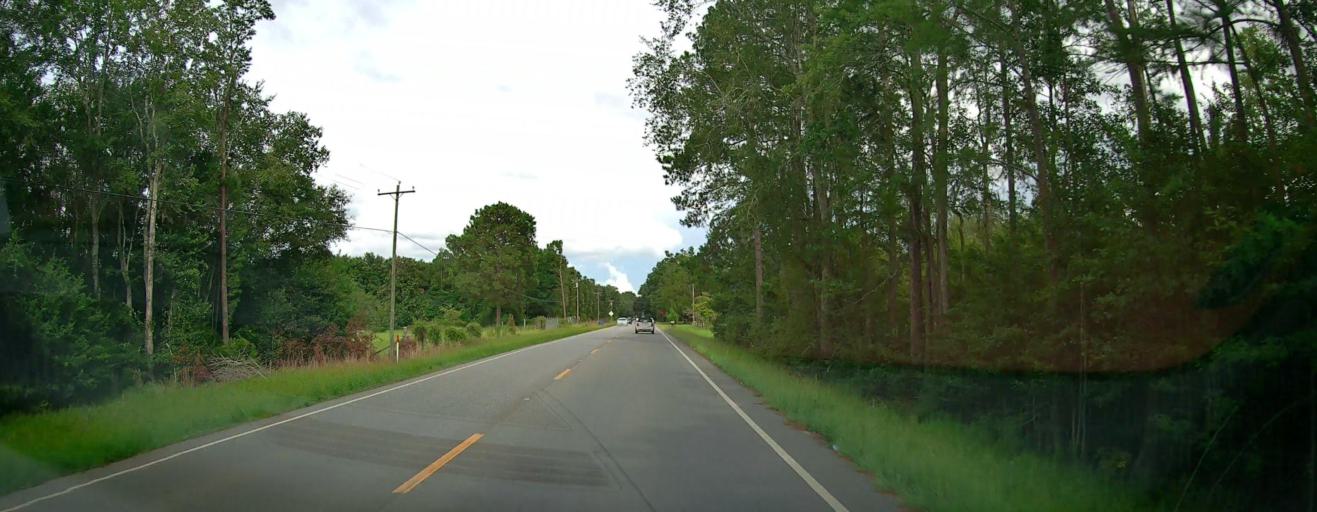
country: US
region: Georgia
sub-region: Wayne County
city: Jesup
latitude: 31.6653
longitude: -81.8677
